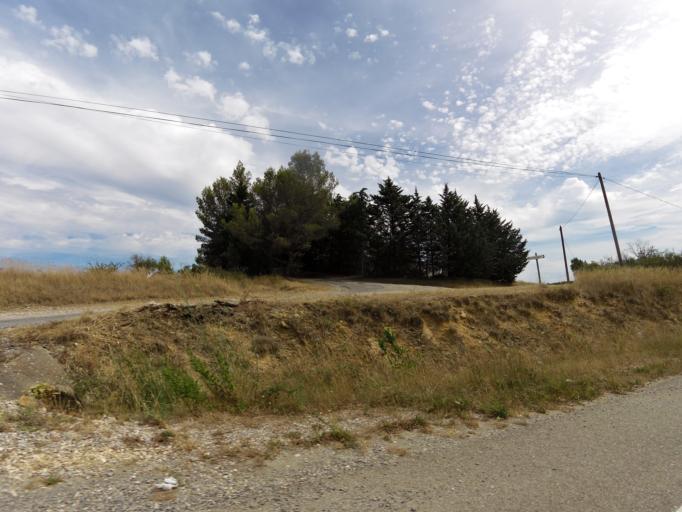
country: FR
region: Languedoc-Roussillon
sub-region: Departement du Gard
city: Saint-Mamert-du-Gard
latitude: 43.8470
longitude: 4.1485
